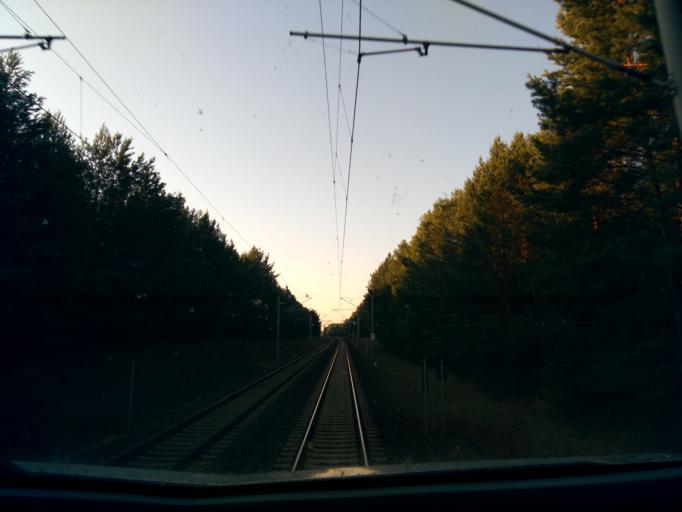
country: DE
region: Brandenburg
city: Gross Koris
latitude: 52.1486
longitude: 13.6595
